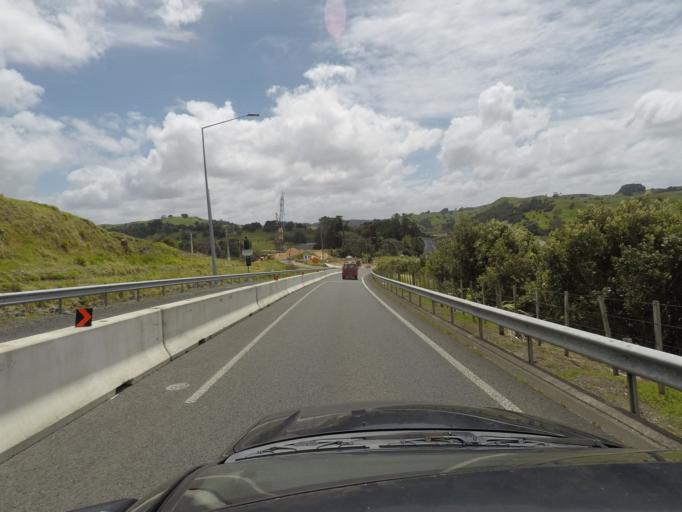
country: NZ
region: Auckland
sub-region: Auckland
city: Warkworth
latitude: -36.5319
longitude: 174.6778
